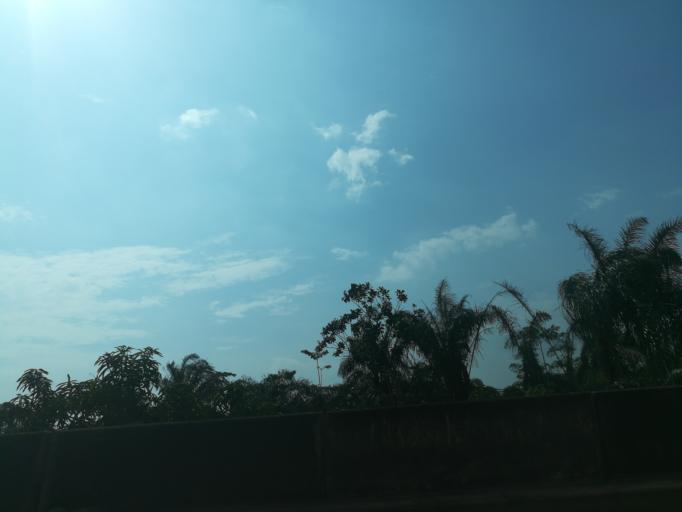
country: NG
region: Lagos
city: Ikorodu
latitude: 6.6250
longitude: 3.6634
